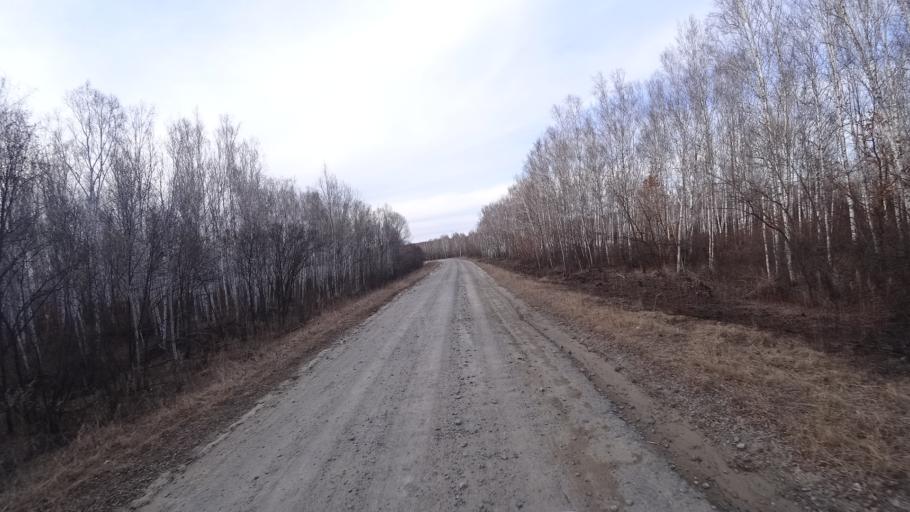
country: RU
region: Amur
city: Bureya
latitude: 50.0133
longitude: 129.7743
